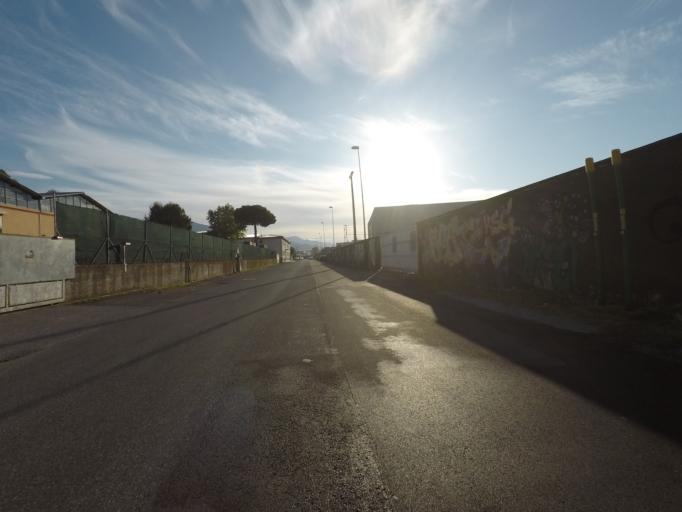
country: IT
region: Tuscany
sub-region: Provincia di Massa-Carrara
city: Massa
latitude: 44.0301
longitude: 10.1094
